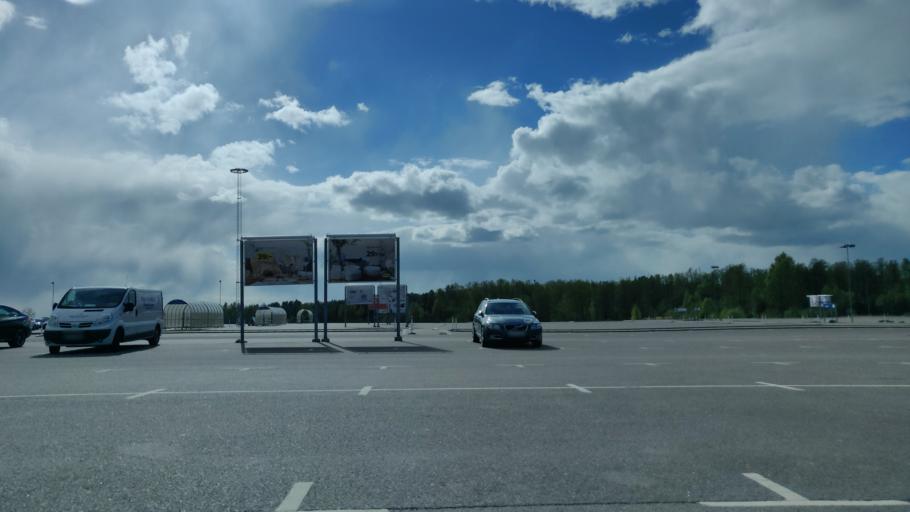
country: SE
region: Vaermland
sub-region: Hammaro Kommun
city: Skoghall
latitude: 59.3800
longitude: 13.4187
